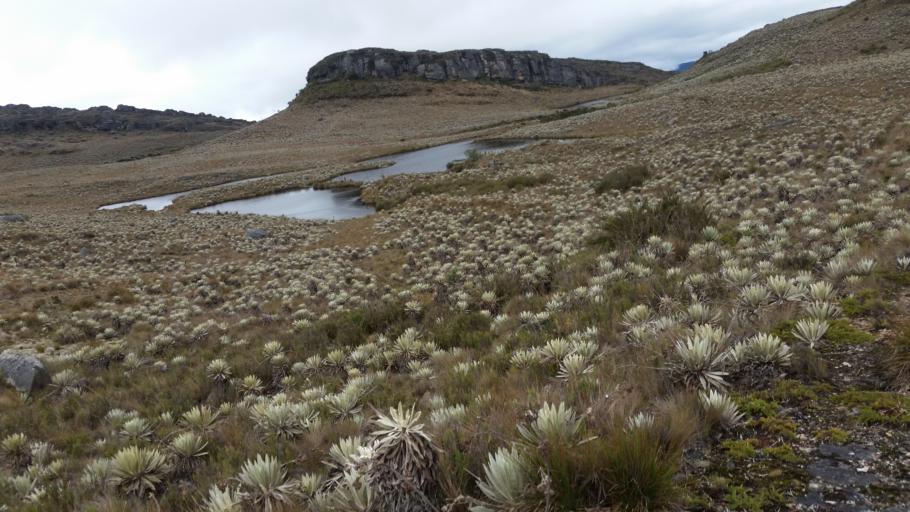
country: CO
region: Cundinamarca
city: Pasca
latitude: 4.3686
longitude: -74.2156
